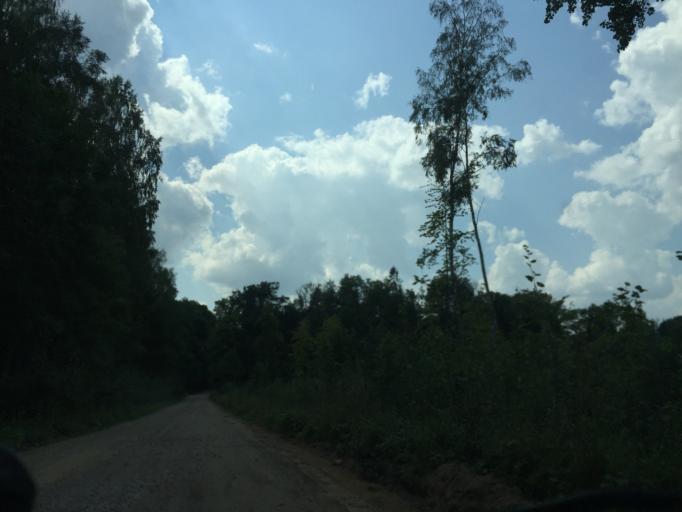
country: LT
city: Zagare
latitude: 56.3752
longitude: 23.1686
